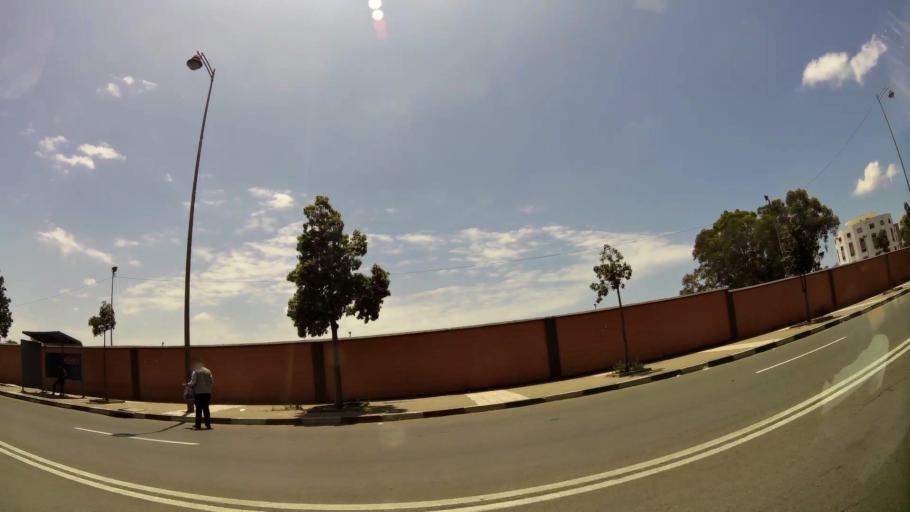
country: MA
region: Gharb-Chrarda-Beni Hssen
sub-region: Kenitra Province
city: Kenitra
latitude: 34.2548
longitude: -6.5602
